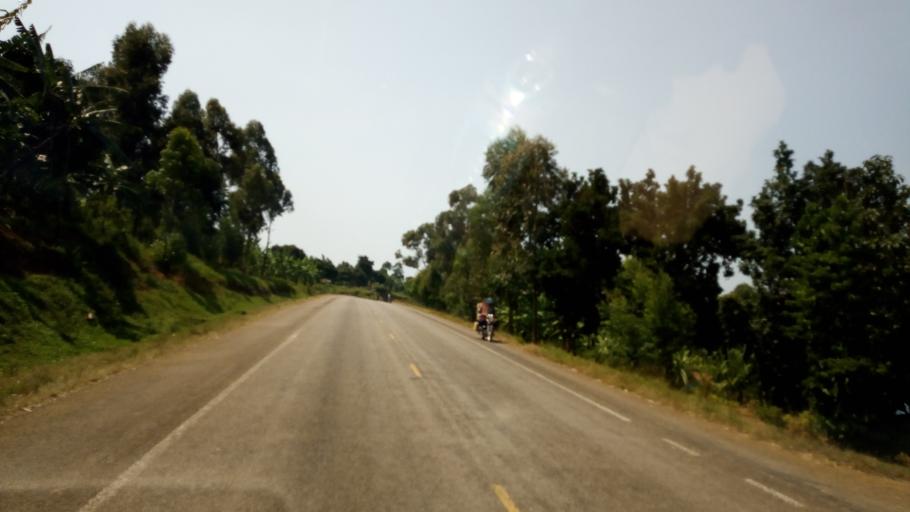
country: UG
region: Western Region
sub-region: Ntungamo District
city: Ntungamo
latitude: -0.8176
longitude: 30.1534
